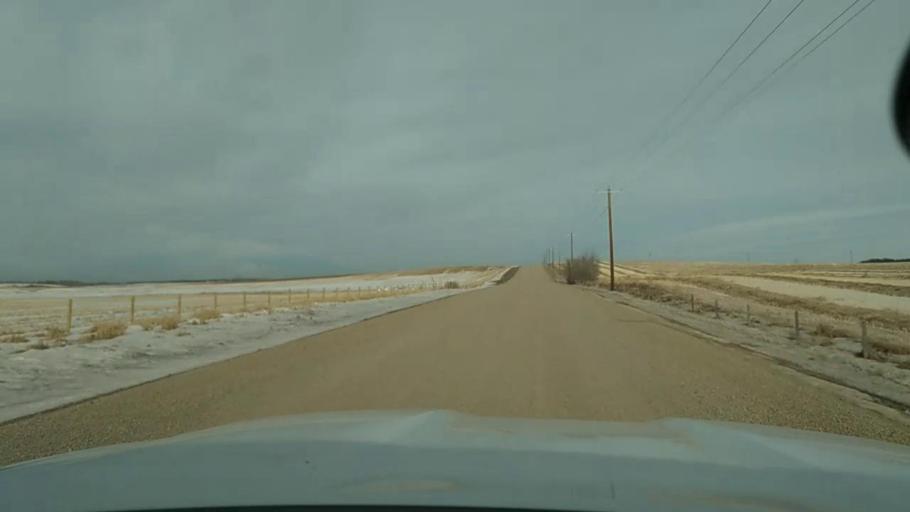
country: CA
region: Alberta
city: Airdrie
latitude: 51.2364
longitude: -113.9118
